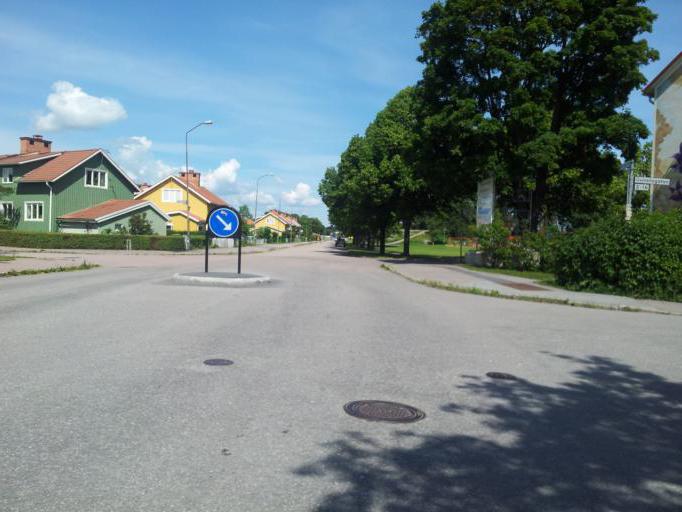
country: SE
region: Uppsala
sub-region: Uppsala Kommun
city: Uppsala
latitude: 59.8598
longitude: 17.6650
